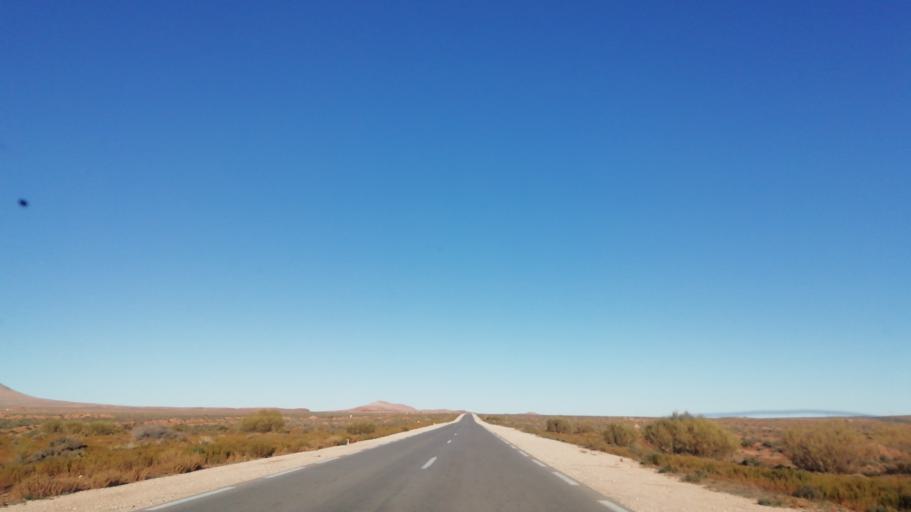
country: DZ
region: El Bayadh
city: El Abiodh Sidi Cheikh
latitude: 33.0979
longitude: 0.2055
